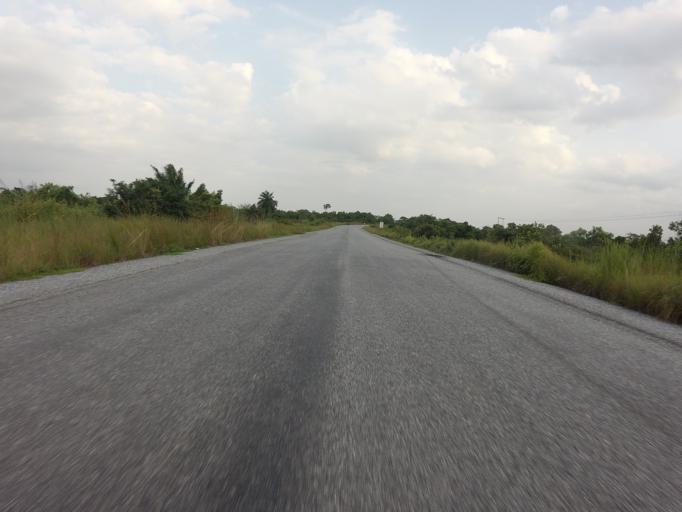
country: GH
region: Volta
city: Ho
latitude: 6.3684
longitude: 0.5341
